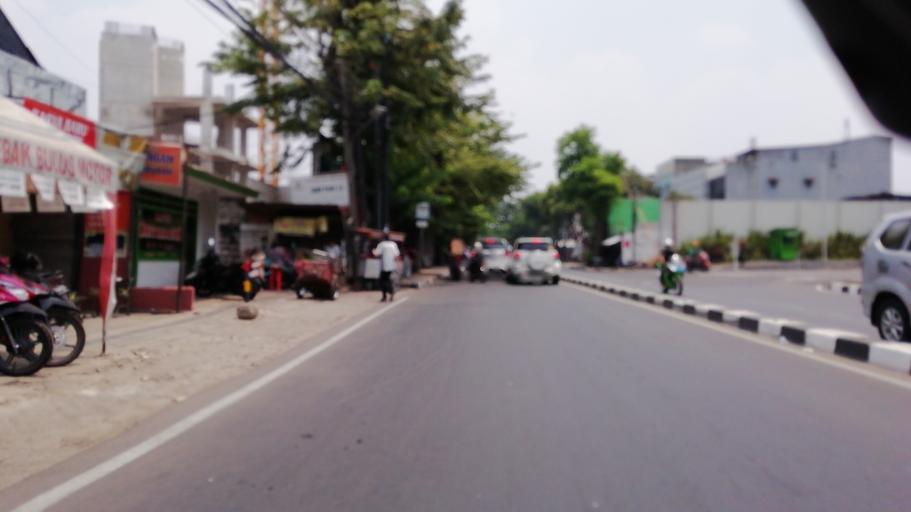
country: ID
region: West Java
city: Pamulang
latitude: -6.3040
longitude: 106.7944
